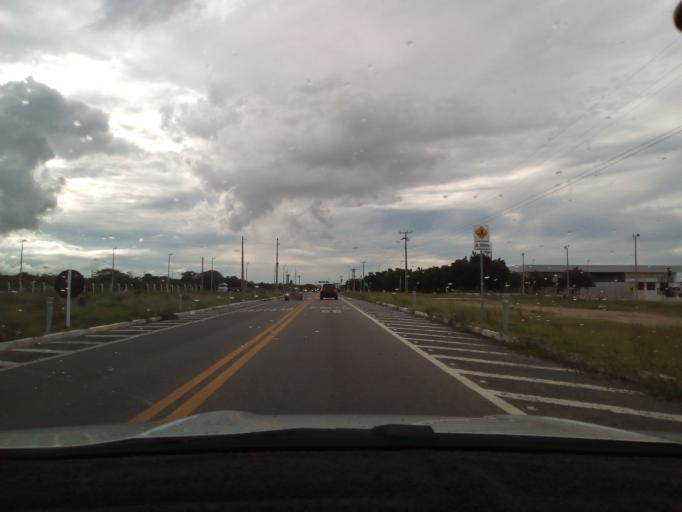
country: BR
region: Ceara
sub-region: Aracati
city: Aracati
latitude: -4.6213
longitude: -37.6492
